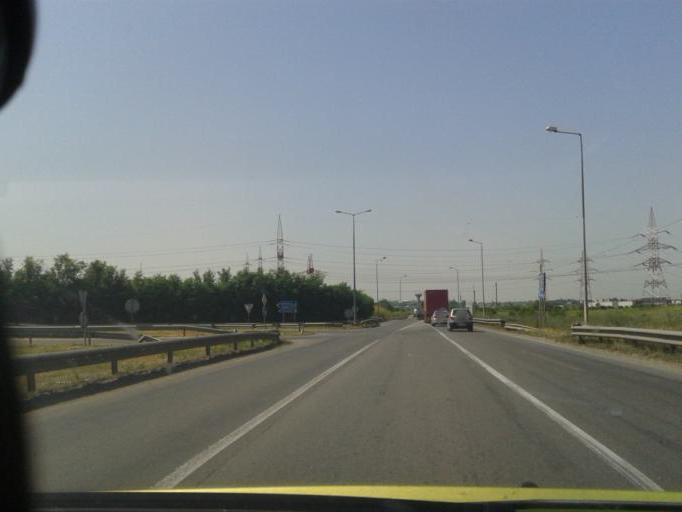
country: RO
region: Ilfov
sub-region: Comuna Glina
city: Catelu
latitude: 44.4066
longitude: 26.2336
